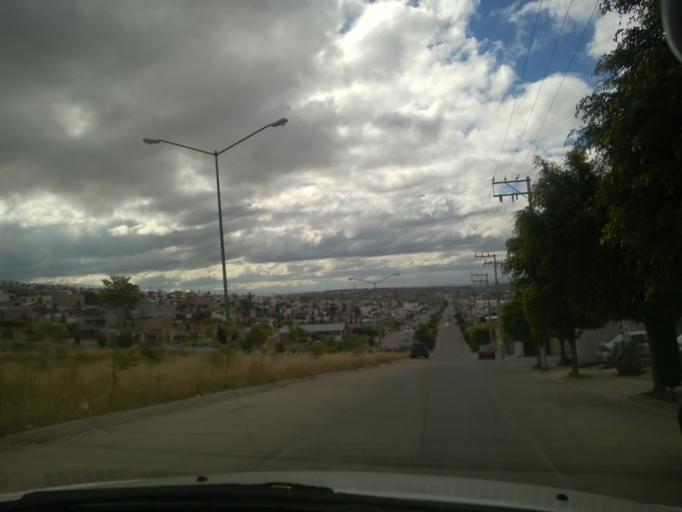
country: MX
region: Guanajuato
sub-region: Leon
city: La Ermita
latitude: 21.1593
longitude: -101.7374
